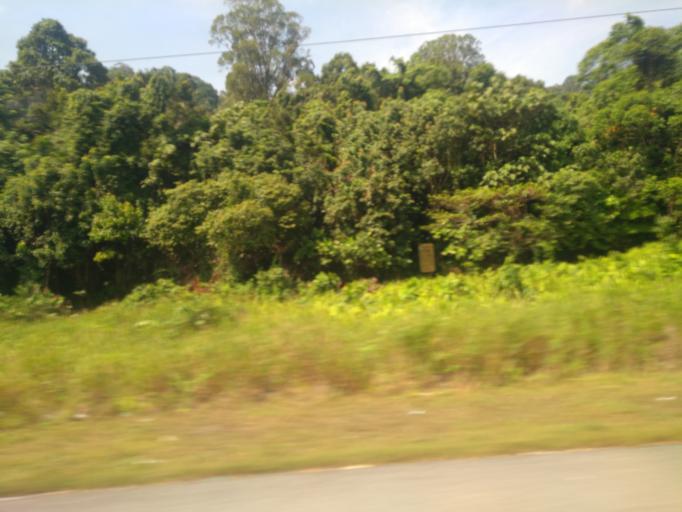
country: MY
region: Sarawak
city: Kuching
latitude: 1.6490
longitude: 110.1826
